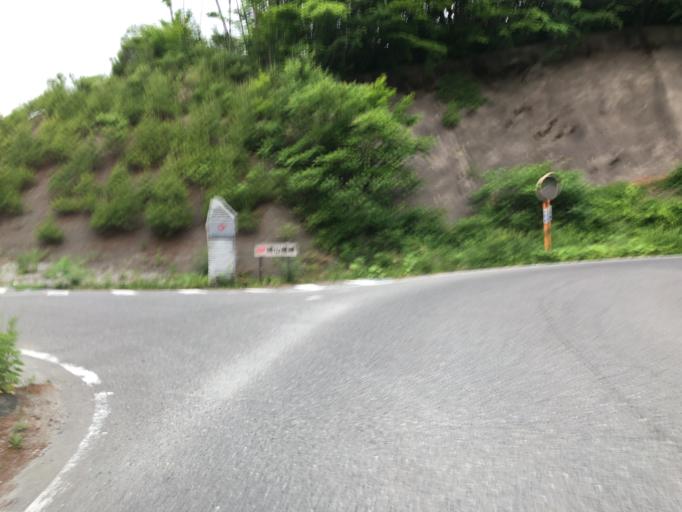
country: JP
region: Fukushima
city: Funehikimachi-funehiki
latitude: 37.3875
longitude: 140.7067
